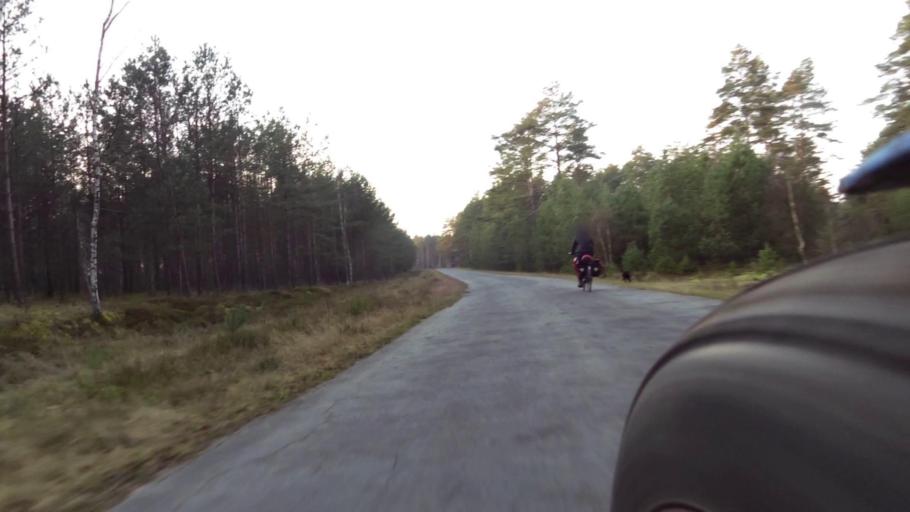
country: PL
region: West Pomeranian Voivodeship
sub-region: Powiat szczecinecki
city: Borne Sulinowo
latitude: 53.5690
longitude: 16.5879
